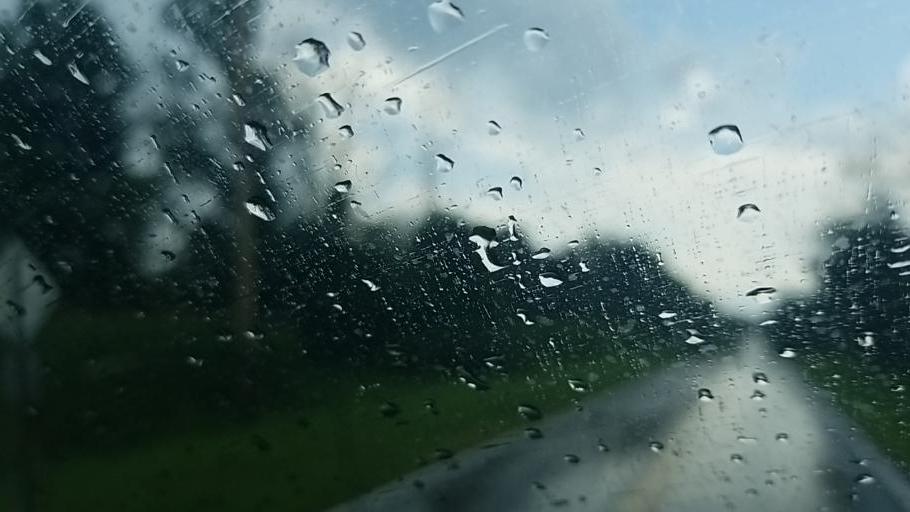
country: US
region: Ohio
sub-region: Lorain County
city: Lagrange
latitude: 41.2222
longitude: -82.0753
